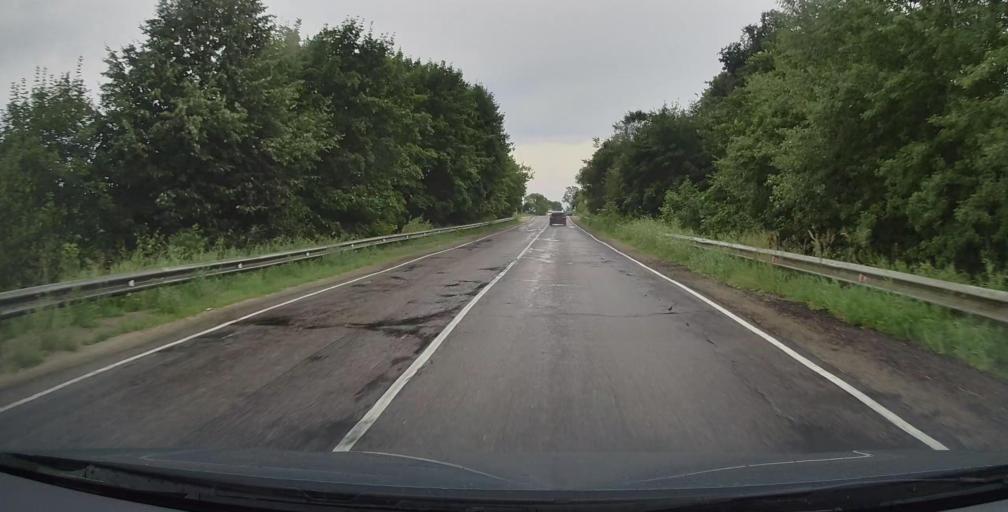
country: RU
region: Tverskaya
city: Kalyazin
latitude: 57.0909
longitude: 37.9273
